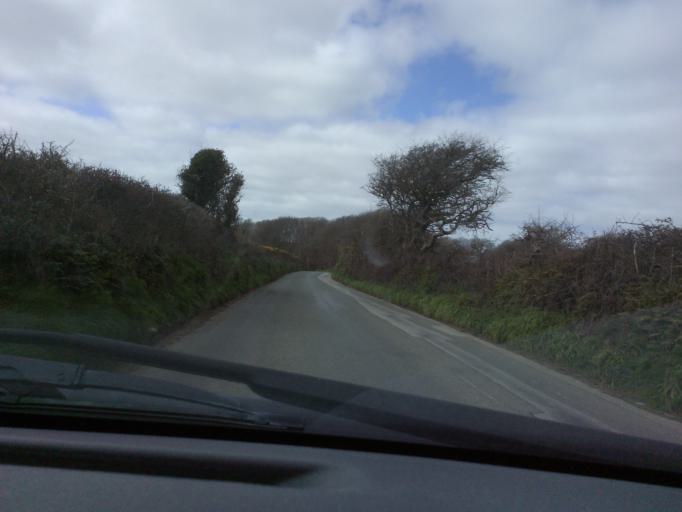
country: GB
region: England
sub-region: Cornwall
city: Penzance
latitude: 50.0787
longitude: -5.5676
